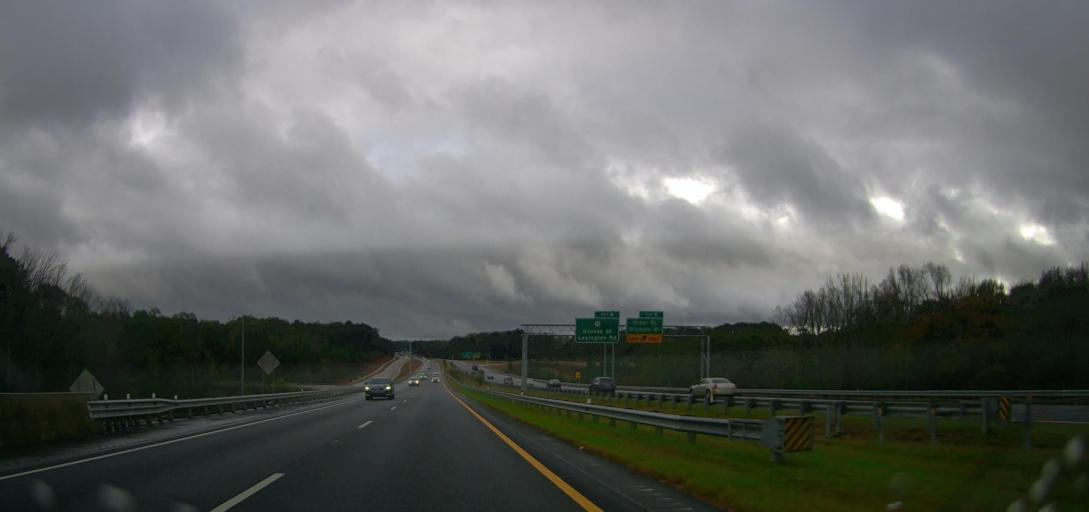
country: US
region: Georgia
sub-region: Clarke County
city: Athens
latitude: 33.9667
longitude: -83.3536
